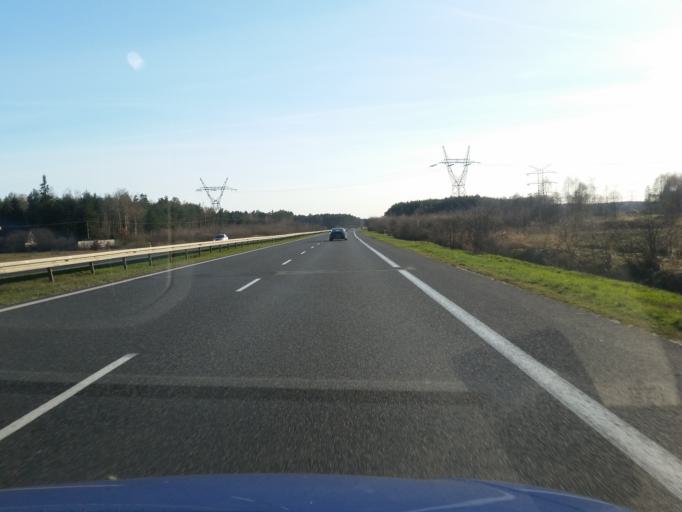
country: PL
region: Lodz Voivodeship
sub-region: Powiat radomszczanski
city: Radomsko
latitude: 51.0505
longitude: 19.3534
